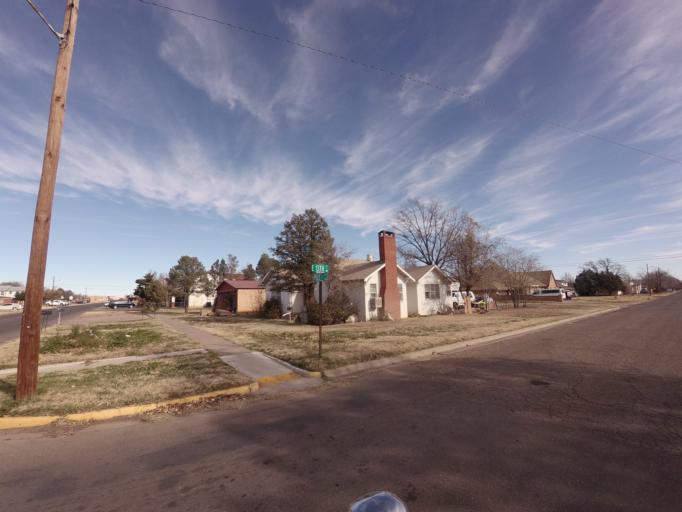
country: US
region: New Mexico
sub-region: Curry County
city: Clovis
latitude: 34.4110
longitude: -103.2039
